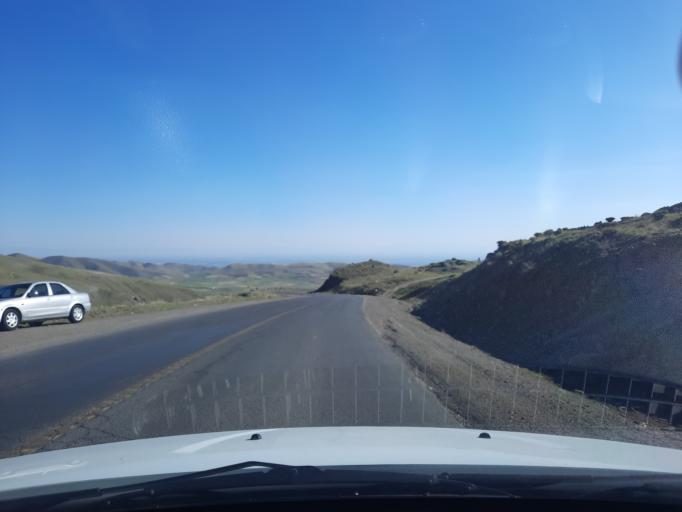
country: IR
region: Qazvin
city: Qazvin
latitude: 36.3671
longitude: 50.2006
